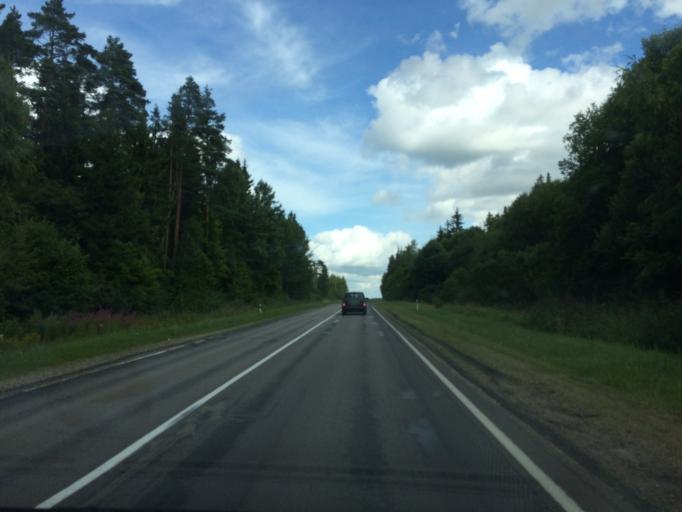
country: LV
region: Rezekne
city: Rezekne
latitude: 56.5965
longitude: 27.4188
